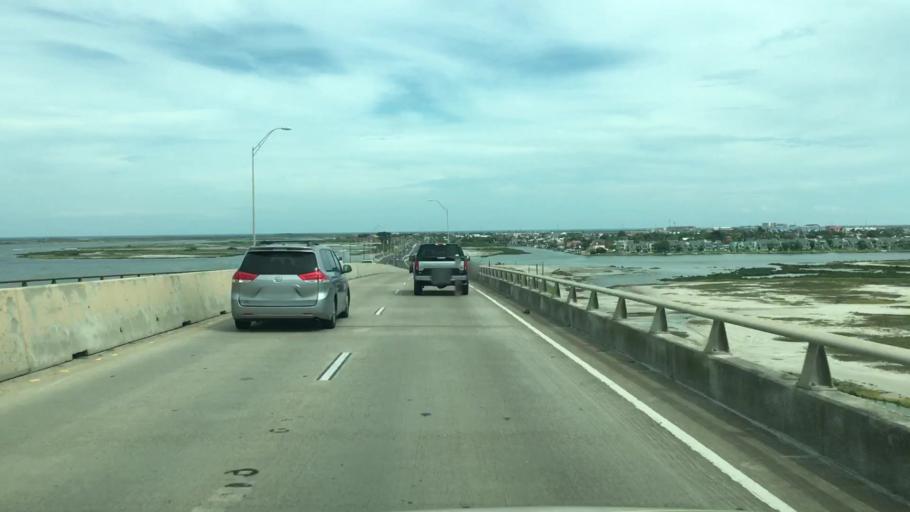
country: US
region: Texas
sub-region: Nueces County
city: Corpus Christi
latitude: 27.6343
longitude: -97.2387
